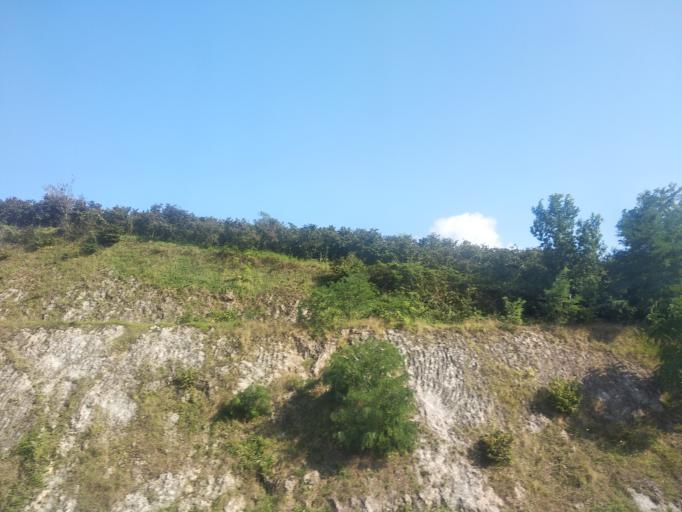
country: TR
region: Ordu
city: Ordu
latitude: 41.0109
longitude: 37.8326
